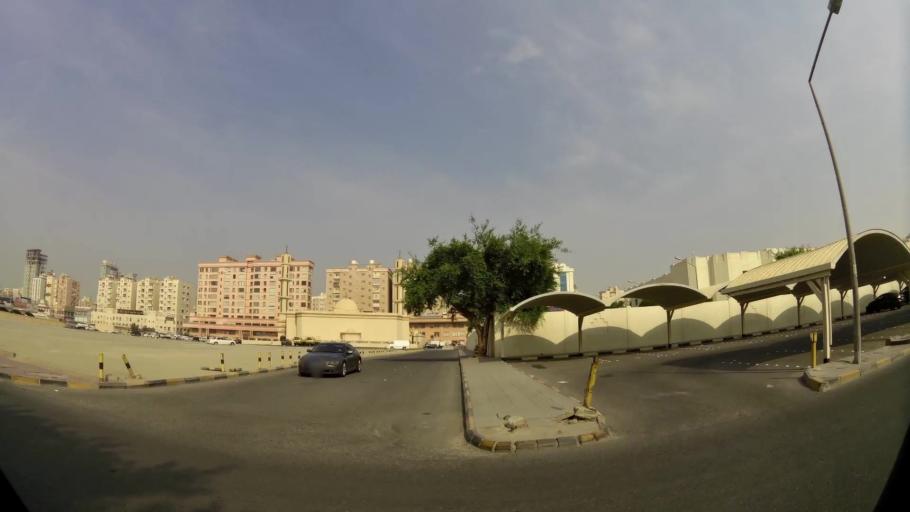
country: KW
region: Al Farwaniyah
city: Al Farwaniyah
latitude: 29.2731
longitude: 47.9612
